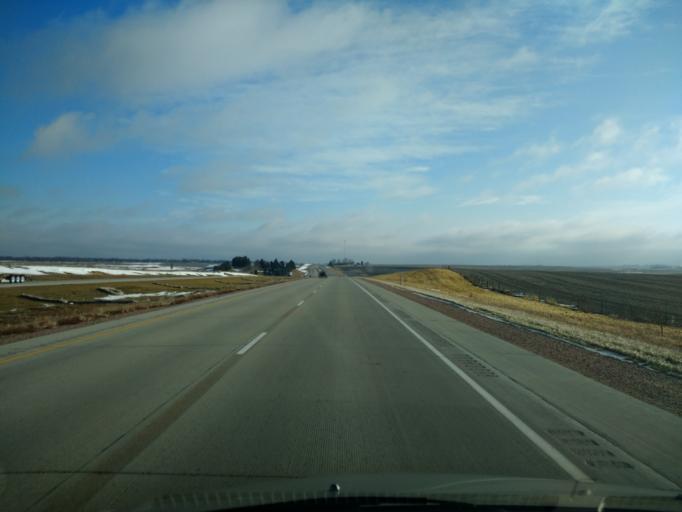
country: US
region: Iowa
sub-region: Ida County
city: Holstein
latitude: 42.4744
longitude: -95.5720
